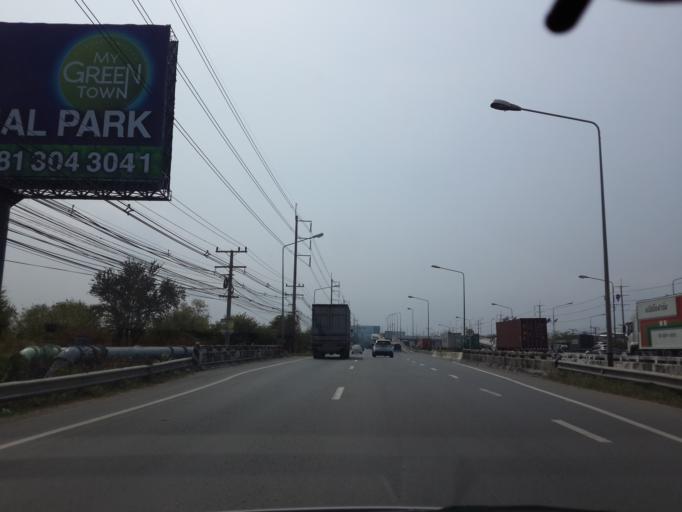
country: TH
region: Chon Buri
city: Chon Buri
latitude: 13.4377
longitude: 101.0013
